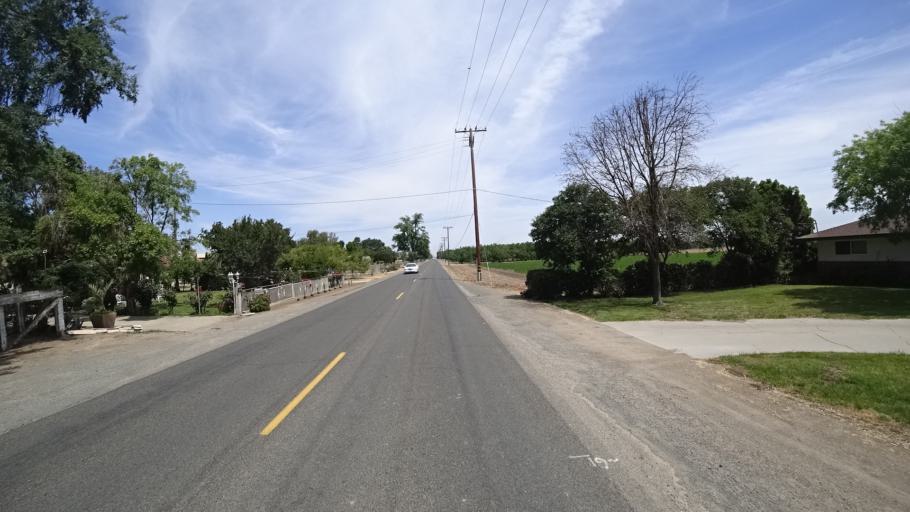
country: US
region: California
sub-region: Kings County
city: Lucerne
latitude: 36.3522
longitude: -119.6910
